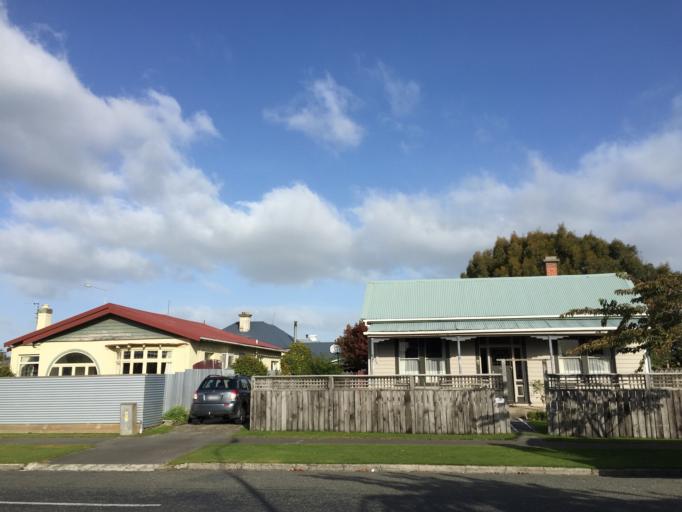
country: NZ
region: Southland
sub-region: Invercargill City
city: Invercargill
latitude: -46.4084
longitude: 168.3691
